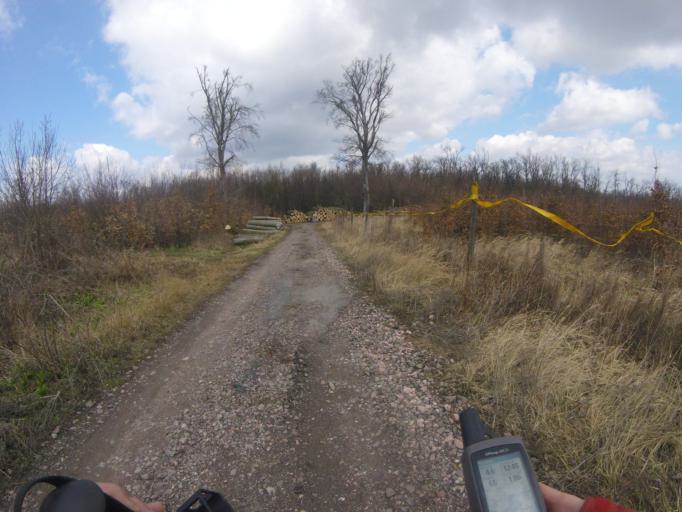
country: HU
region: Komarom-Esztergom
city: Tardos
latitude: 47.6824
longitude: 18.5010
